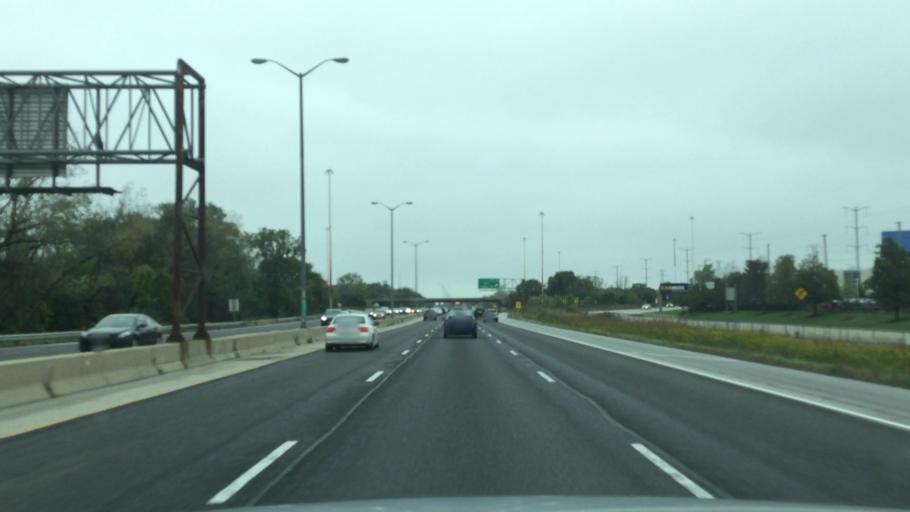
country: US
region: Illinois
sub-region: Cook County
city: Northfield
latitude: 42.1197
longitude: -87.7799
